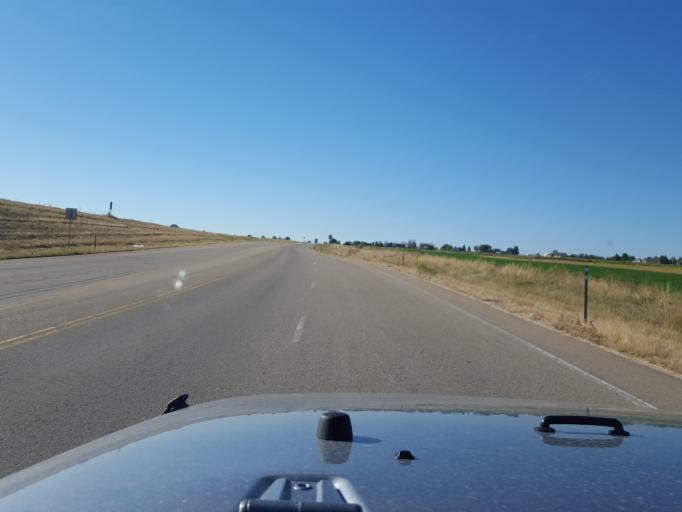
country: US
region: Colorado
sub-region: Weld County
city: Firestone
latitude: 40.1307
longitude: -104.9812
